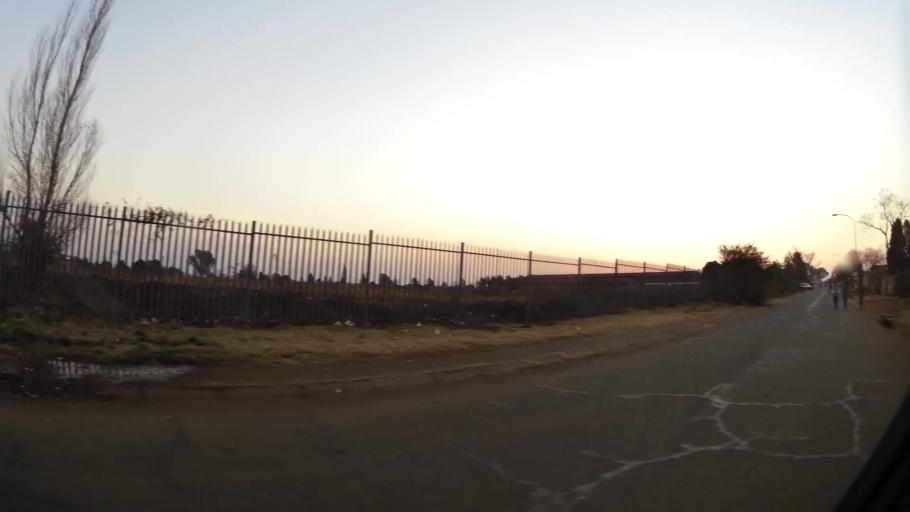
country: ZA
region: Gauteng
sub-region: City of Johannesburg Metropolitan Municipality
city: Soweto
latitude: -26.2922
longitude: 27.8758
